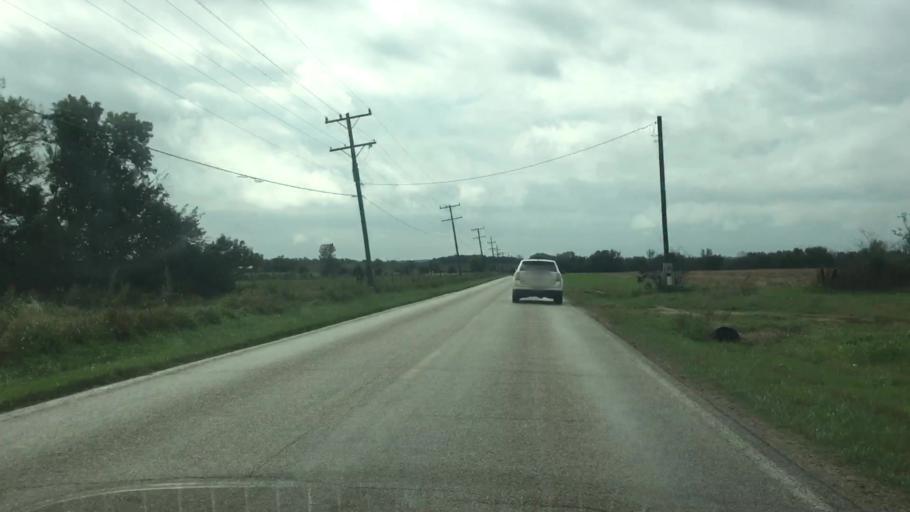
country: US
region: Kansas
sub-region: Allen County
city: Humboldt
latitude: 37.8569
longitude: -95.4369
